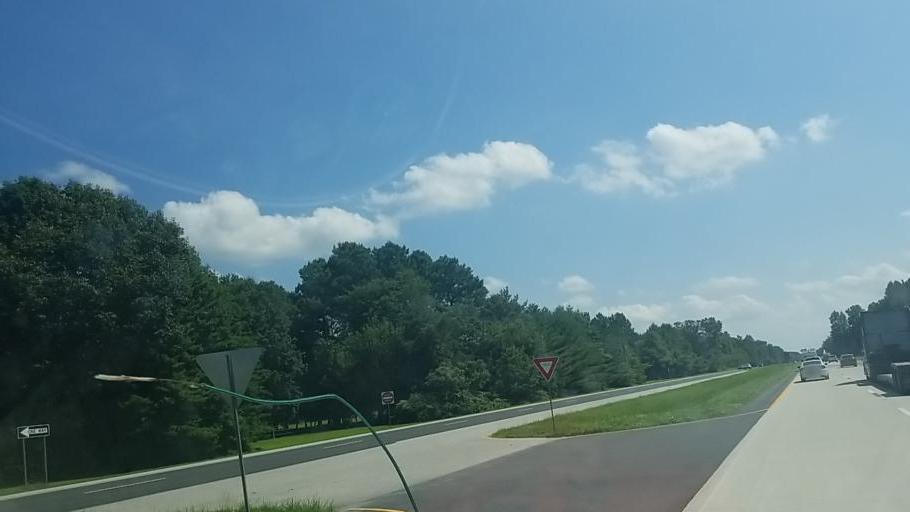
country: US
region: Delaware
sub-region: Sussex County
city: Milford
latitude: 38.8442
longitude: -75.4393
